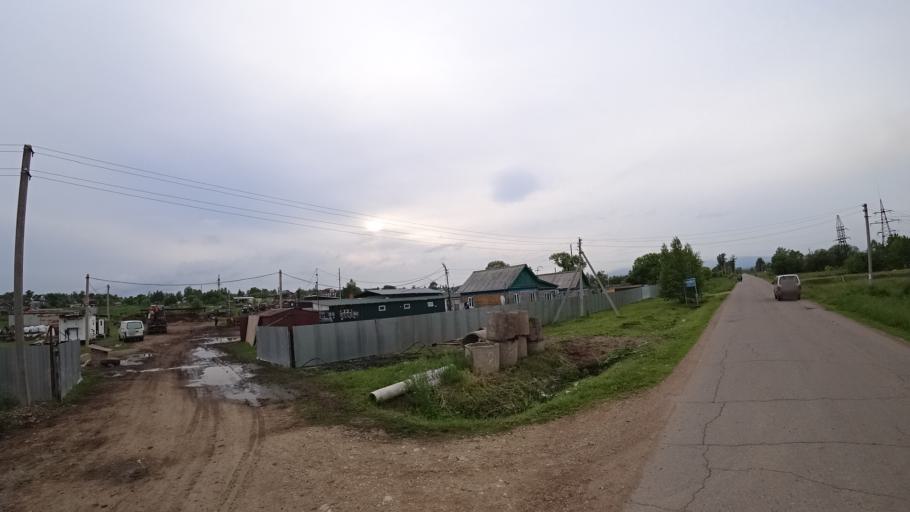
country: RU
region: Primorskiy
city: Novosysoyevka
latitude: 44.2324
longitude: 133.3711
